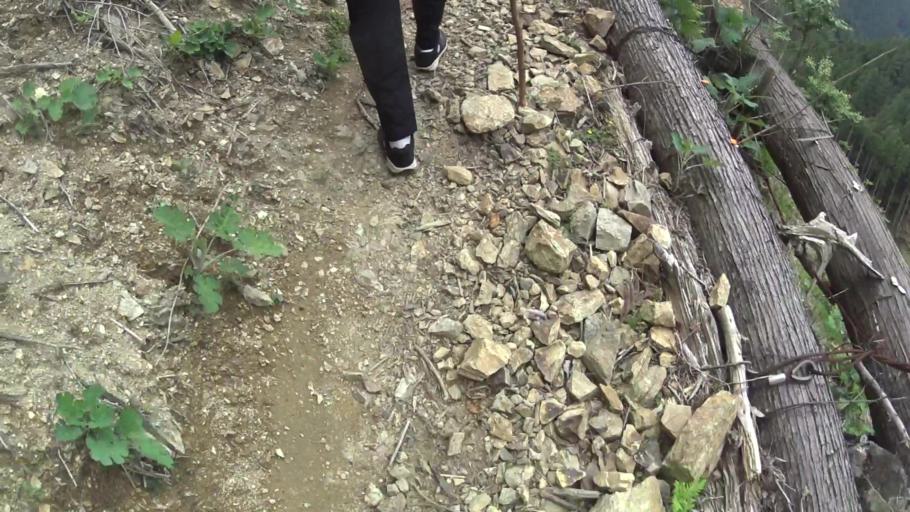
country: JP
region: Nara
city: Yoshino-cho
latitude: 34.3393
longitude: 135.8814
